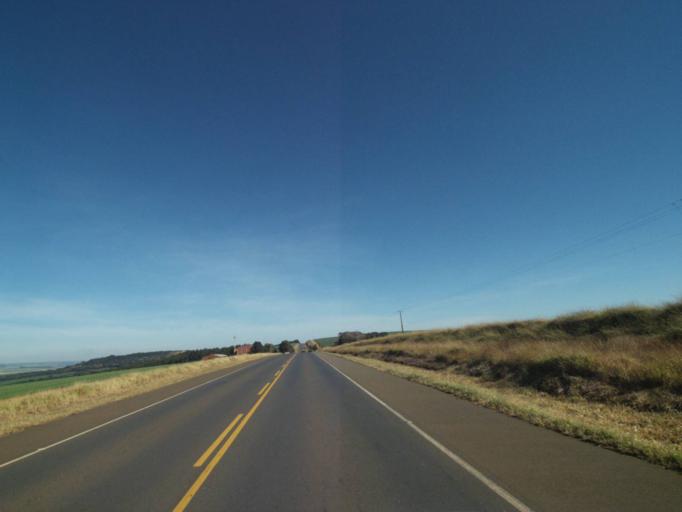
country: BR
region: Parana
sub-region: Tibagi
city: Tibagi
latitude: -24.3557
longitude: -50.3168
